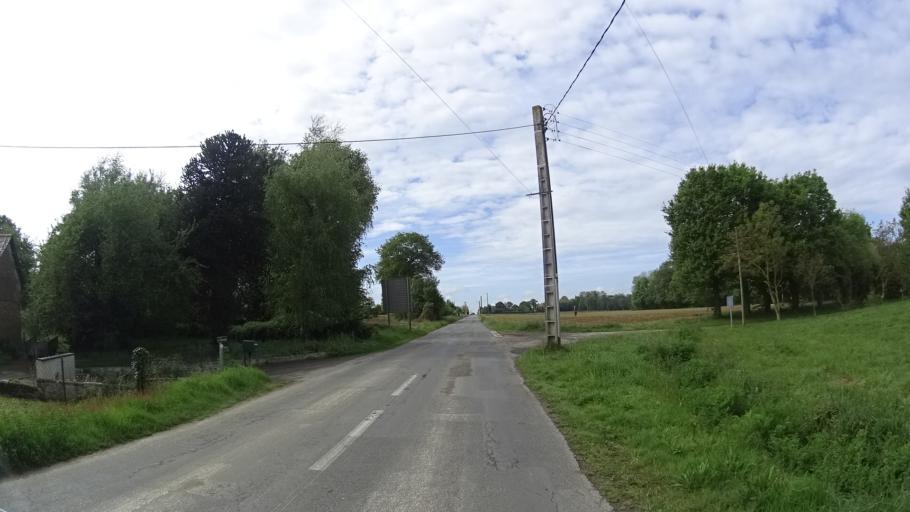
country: FR
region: Brittany
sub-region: Departement d'Ille-et-Vilaine
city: Mordelles
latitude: 48.0843
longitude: -1.8418
